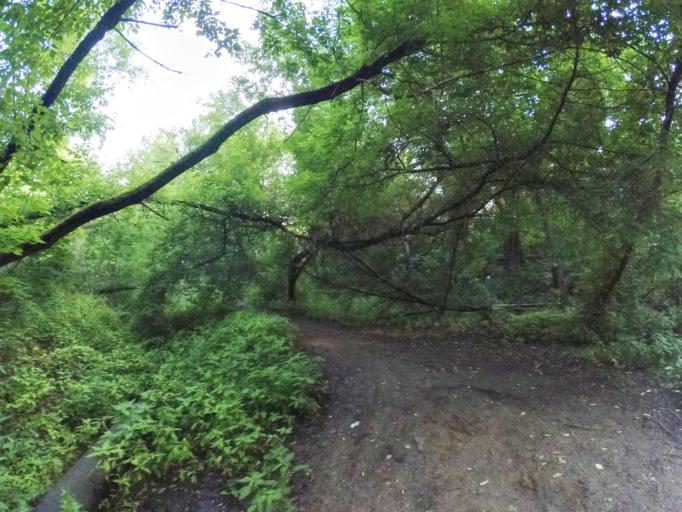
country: RU
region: Moscow
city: Shchukino
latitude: 55.7968
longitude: 37.4487
